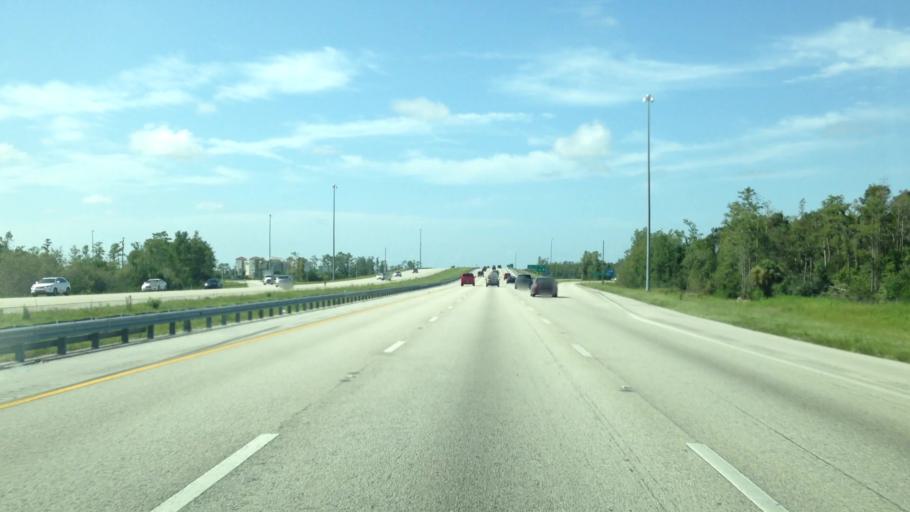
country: US
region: Florida
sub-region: Lee County
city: Tice
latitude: 26.6408
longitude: -81.8014
